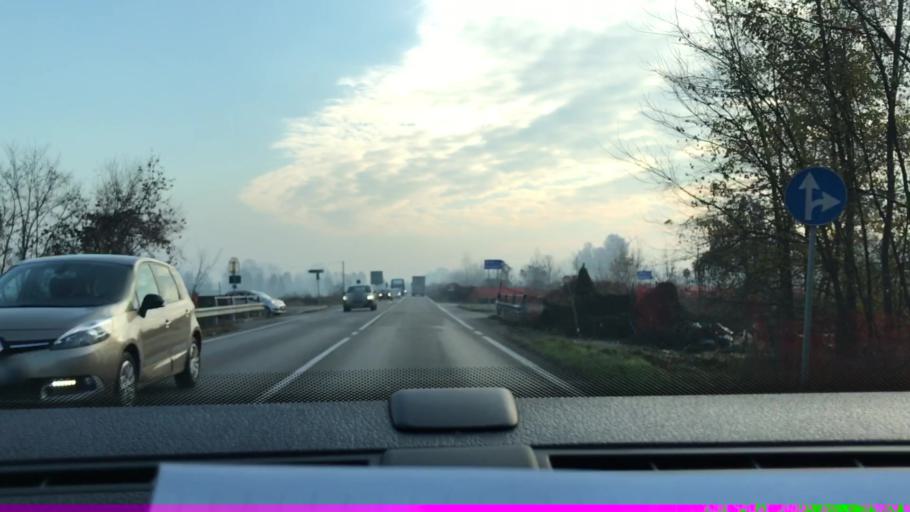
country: IT
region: Lombardy
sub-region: Provincia di Brescia
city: Torbole Casaglia
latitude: 45.4866
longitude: 10.1059
